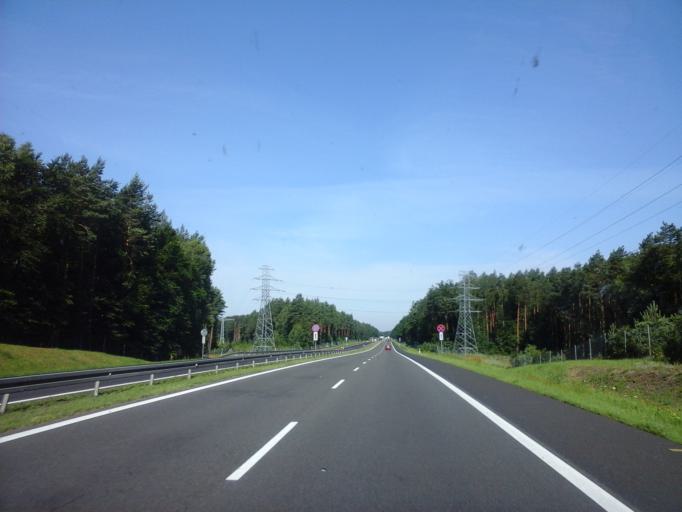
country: PL
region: West Pomeranian Voivodeship
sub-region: Powiat gryfinski
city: Stare Czarnowo
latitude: 53.3567
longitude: 14.7886
